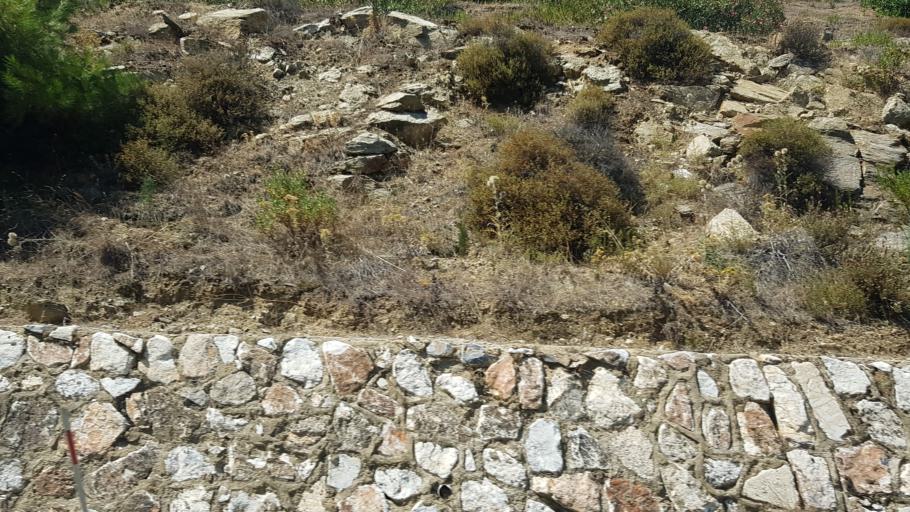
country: TR
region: Aydin
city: Akcaova
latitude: 37.5071
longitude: 28.1022
